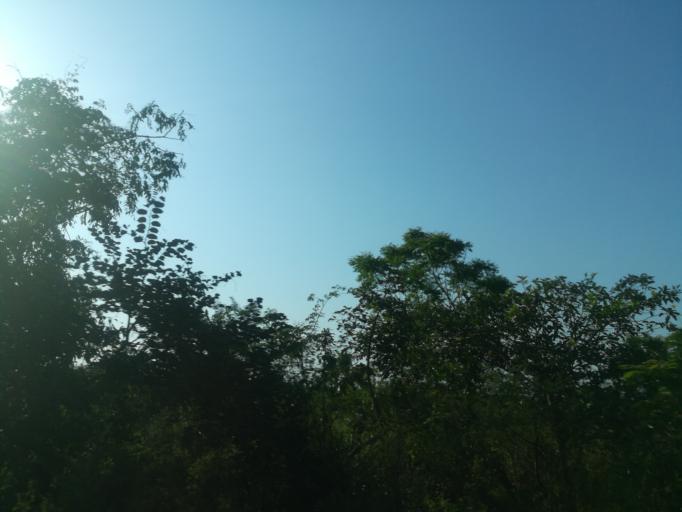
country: NG
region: Ogun
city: Abeokuta
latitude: 7.2073
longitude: 3.2914
